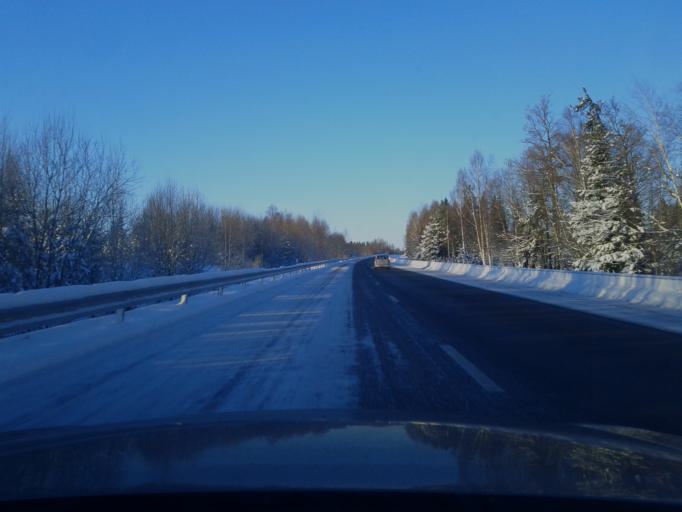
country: SE
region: Uppsala
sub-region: Alvkarleby Kommun
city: AElvkarleby
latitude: 60.4753
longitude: 17.3794
